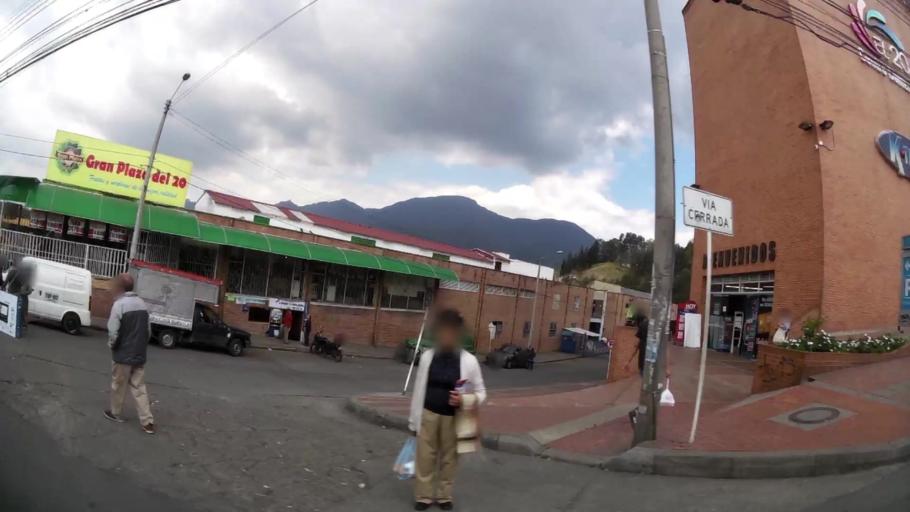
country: CO
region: Bogota D.C.
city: Bogota
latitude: 4.5695
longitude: -74.0937
